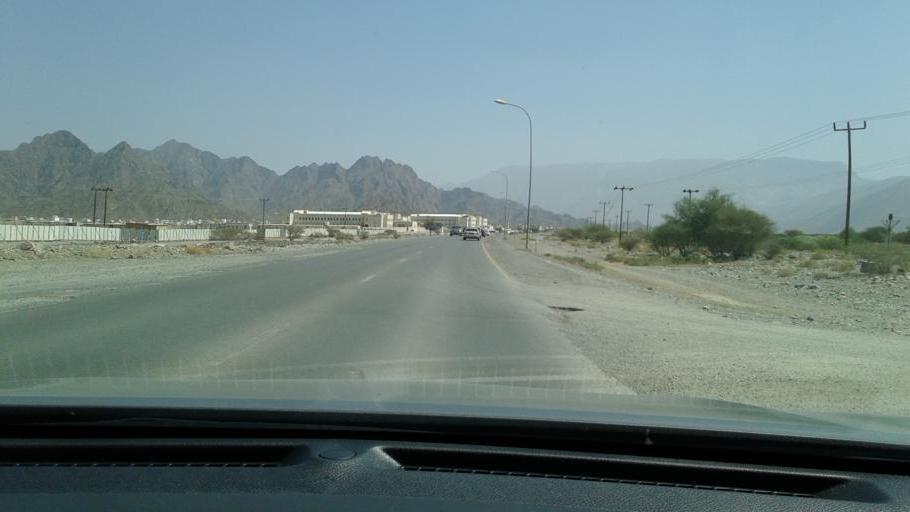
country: OM
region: Al Batinah
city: Rustaq
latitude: 23.3632
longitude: 57.4761
